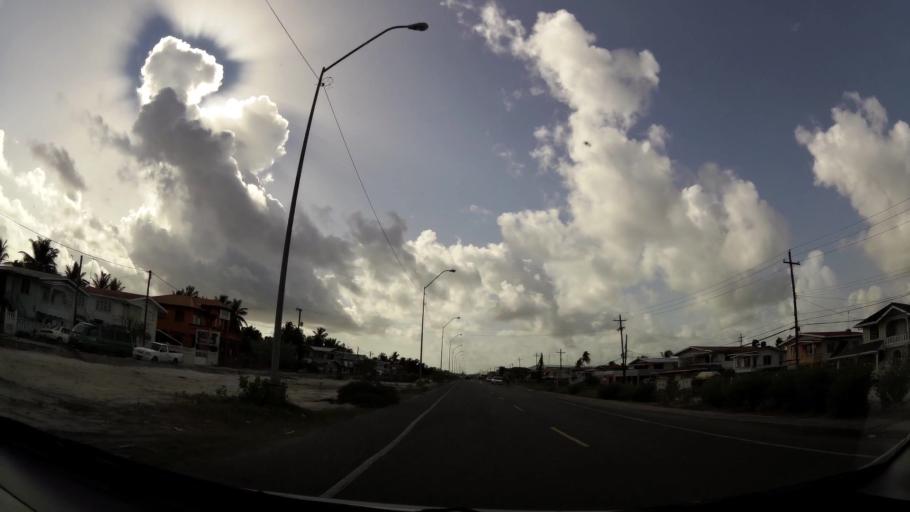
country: GY
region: Demerara-Mahaica
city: Georgetown
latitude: 6.8055
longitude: -58.0498
